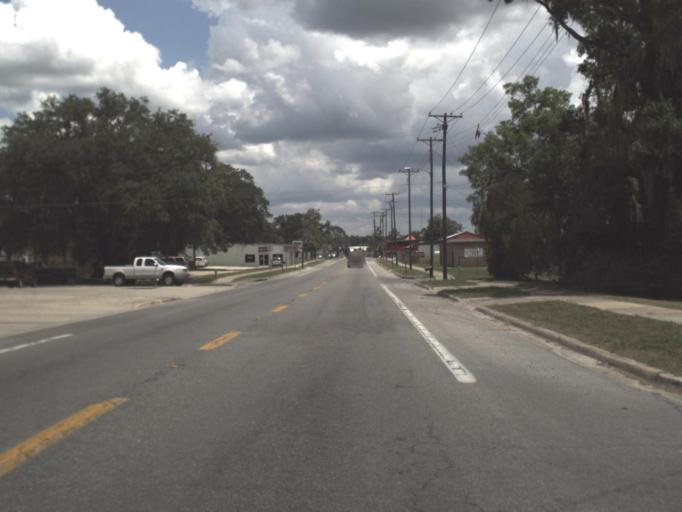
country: US
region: Florida
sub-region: Taylor County
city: Perry
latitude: 30.1116
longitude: -83.5876
